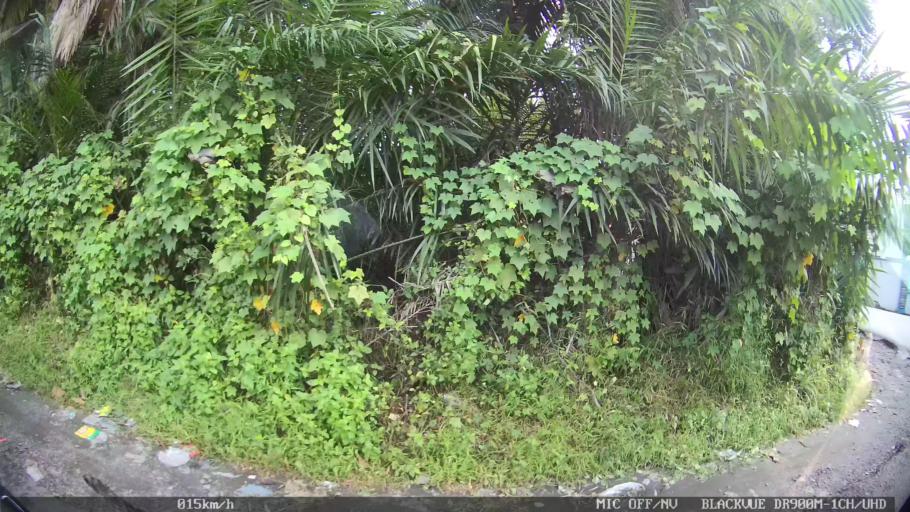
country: ID
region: North Sumatra
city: Medan
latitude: 3.6216
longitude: 98.7141
